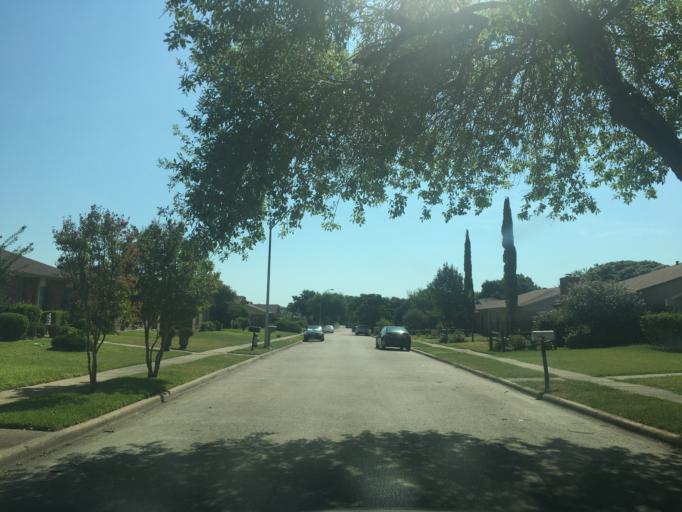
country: US
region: Texas
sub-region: Dallas County
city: Garland
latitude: 32.8533
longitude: -96.6647
